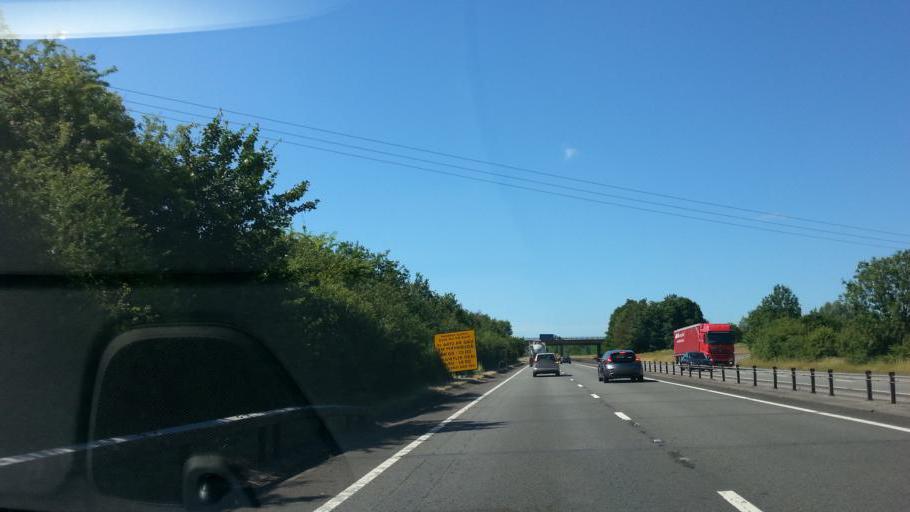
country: GB
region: Wales
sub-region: Monmouthshire
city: Usk
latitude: 51.7060
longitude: -2.8705
